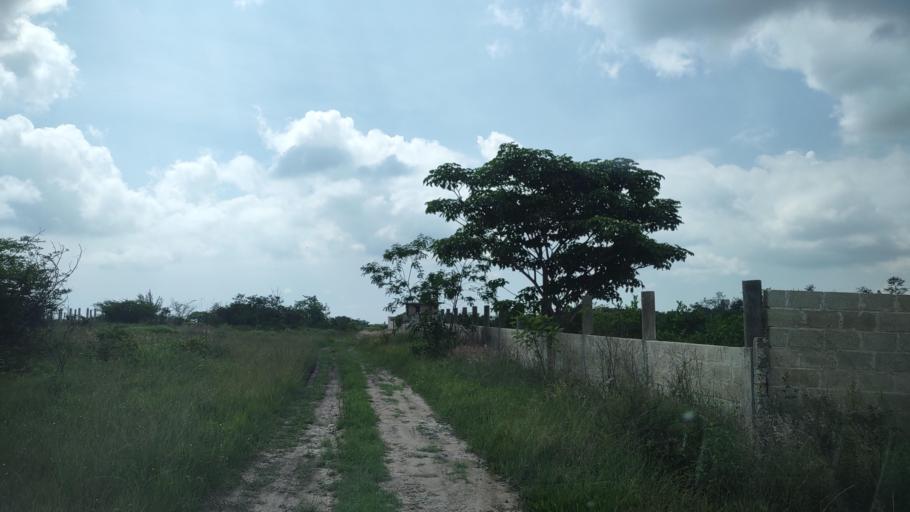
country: MX
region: Veracruz
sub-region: Emiliano Zapata
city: Dos Rios
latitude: 19.4612
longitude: -96.7911
